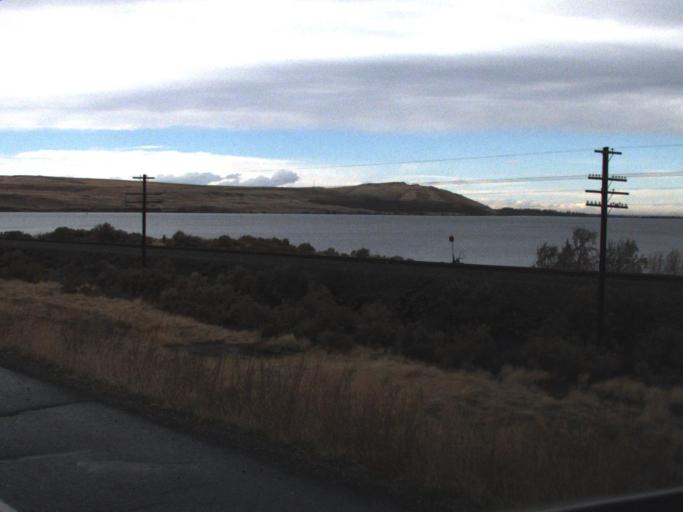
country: US
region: Washington
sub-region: Benton County
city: Finley
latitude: 46.0568
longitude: -118.9232
